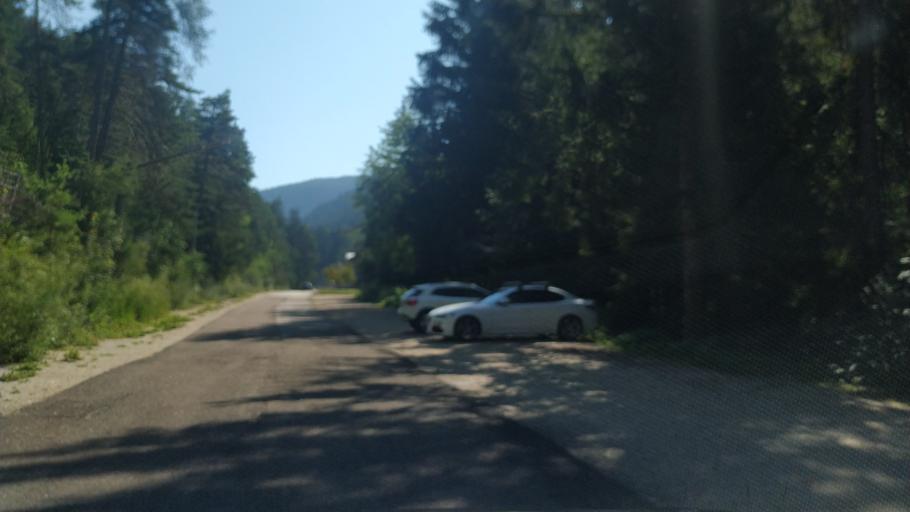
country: IT
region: Trentino-Alto Adige
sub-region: Provincia di Trento
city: Malosco
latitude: 46.4461
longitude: 11.1479
